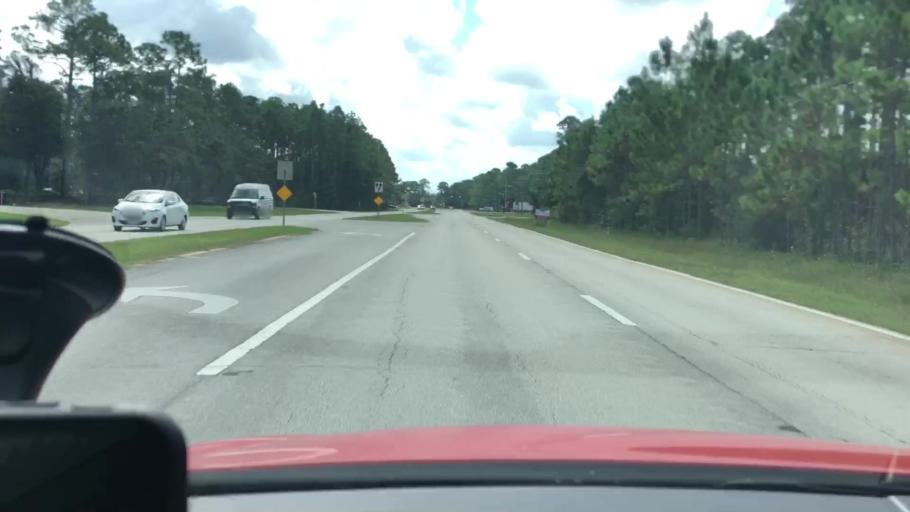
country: US
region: Florida
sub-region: Volusia County
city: Holly Hill
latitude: 29.2122
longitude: -81.0741
